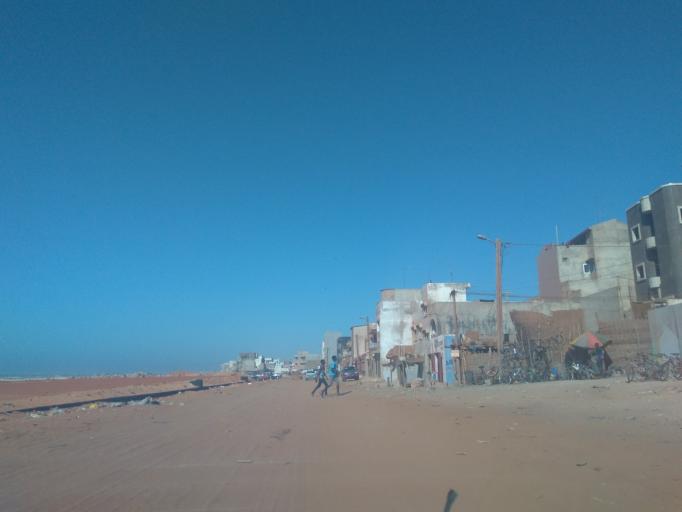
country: SN
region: Dakar
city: Pikine
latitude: 14.7671
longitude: -17.4379
